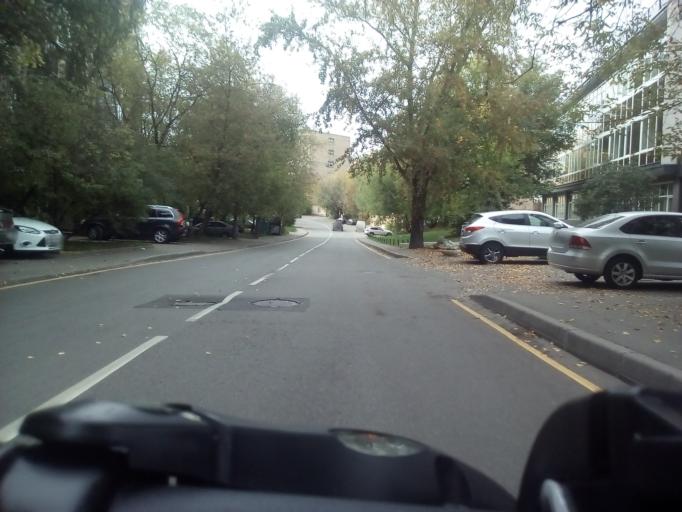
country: RU
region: Moscow
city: Rostokino
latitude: 55.8229
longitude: 37.6658
